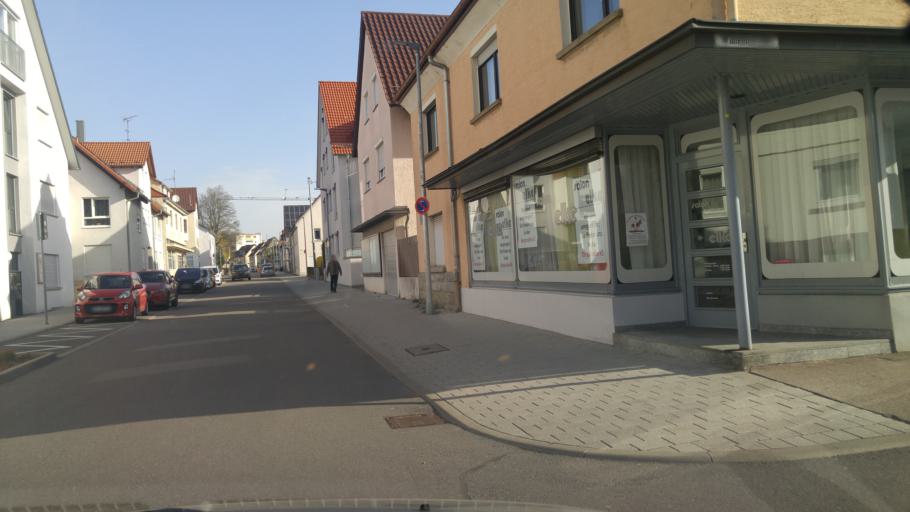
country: DE
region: Baden-Wuerttemberg
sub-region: Regierungsbezirk Stuttgart
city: Leonberg
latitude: 48.7904
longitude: 9.0056
